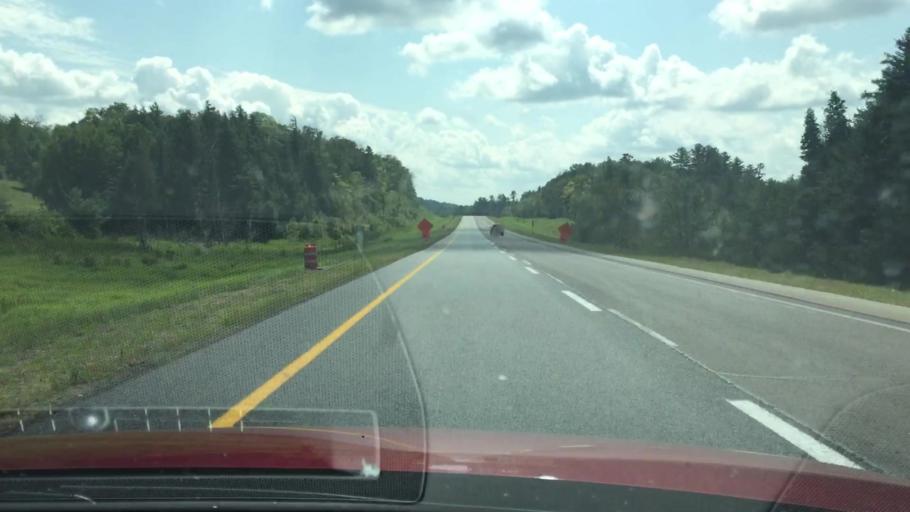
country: US
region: Maine
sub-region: Penobscot County
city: Medway
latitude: 45.7255
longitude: -68.4739
